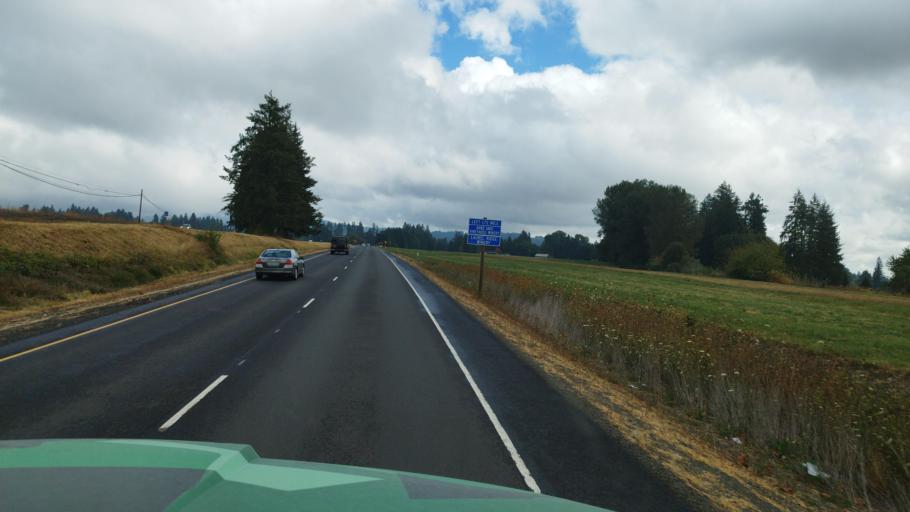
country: US
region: Oregon
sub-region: Yamhill County
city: Lafayette
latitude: 45.2423
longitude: -123.1327
